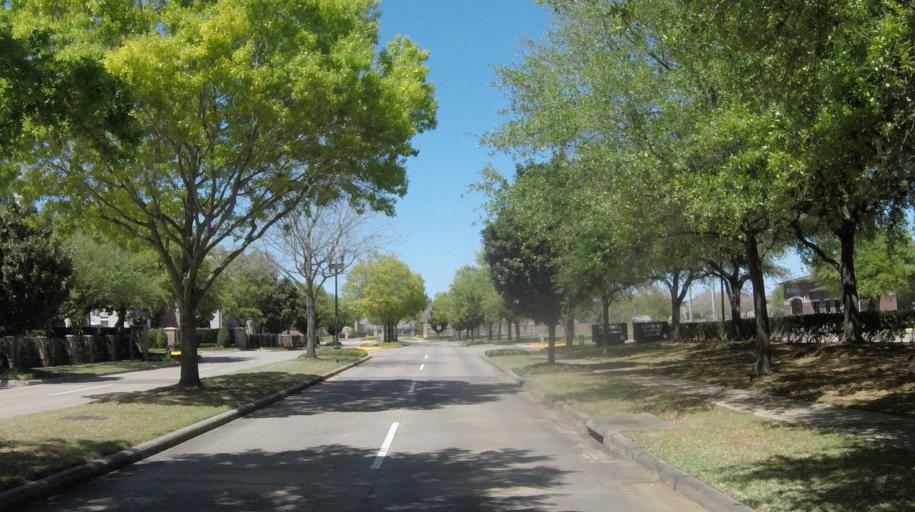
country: US
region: Texas
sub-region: Fort Bend County
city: Sugar Land
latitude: 29.6059
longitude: -95.6214
